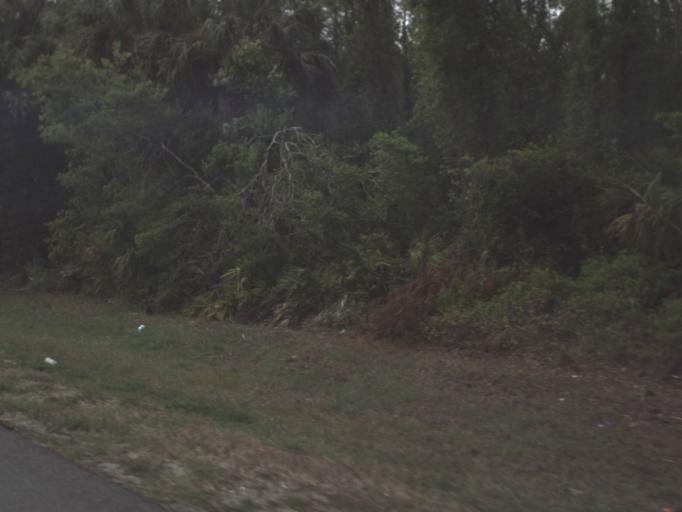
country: US
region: Florida
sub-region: Flagler County
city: Bunnell
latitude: 29.4673
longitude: -81.2965
